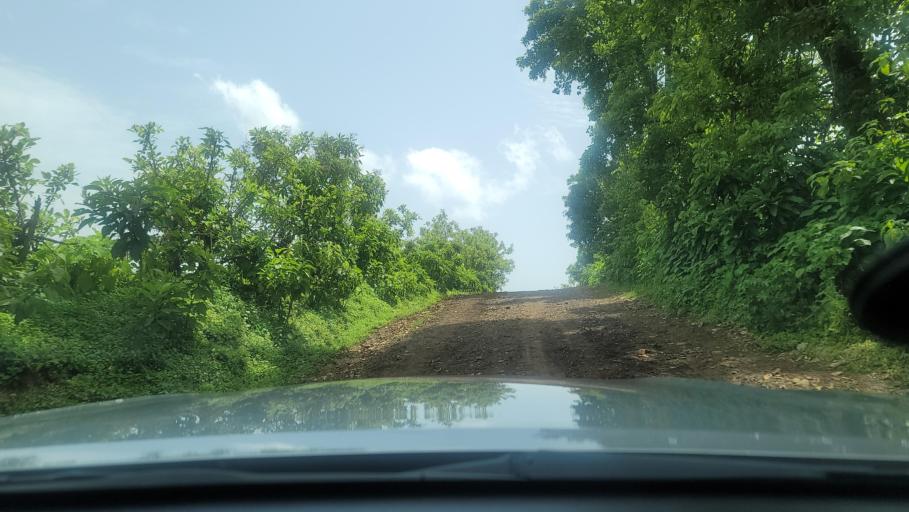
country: ET
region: Oromiya
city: Agaro
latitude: 7.8366
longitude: 36.4072
